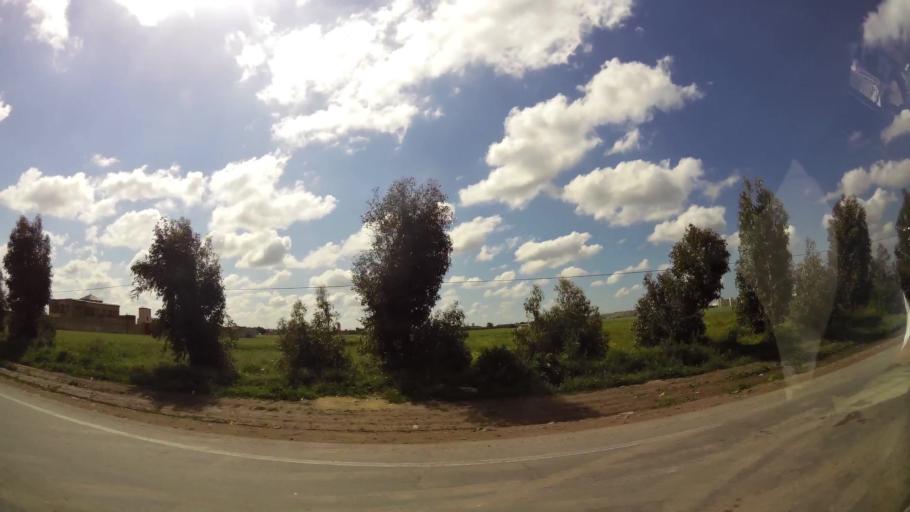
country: MA
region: Grand Casablanca
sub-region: Mediouna
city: Mediouna
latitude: 33.4277
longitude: -7.5231
